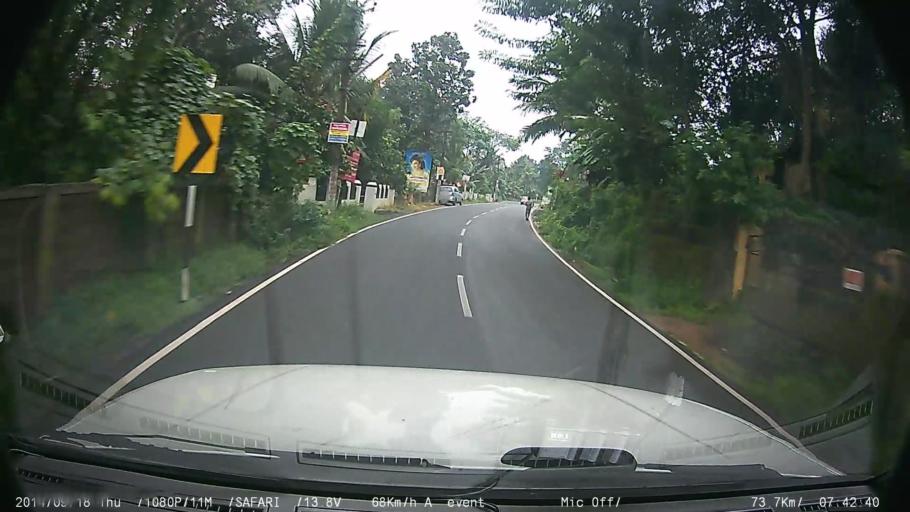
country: IN
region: Kerala
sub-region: Kottayam
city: Changanacheri
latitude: 9.4689
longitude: 76.5780
